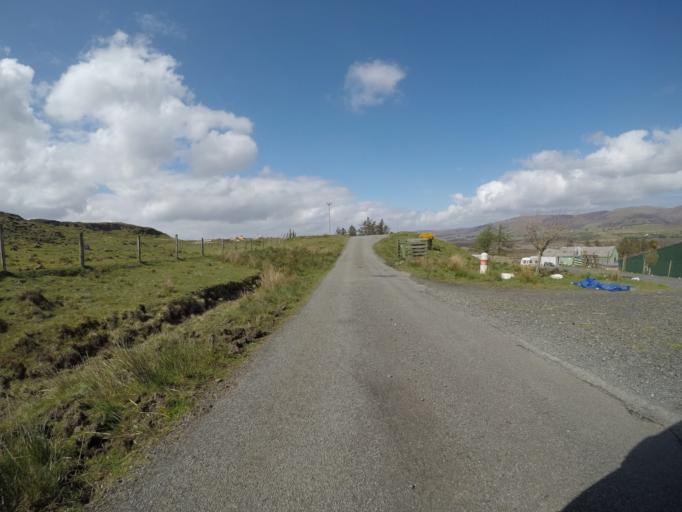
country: GB
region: Scotland
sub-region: Highland
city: Isle of Skye
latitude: 57.4254
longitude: -6.2690
